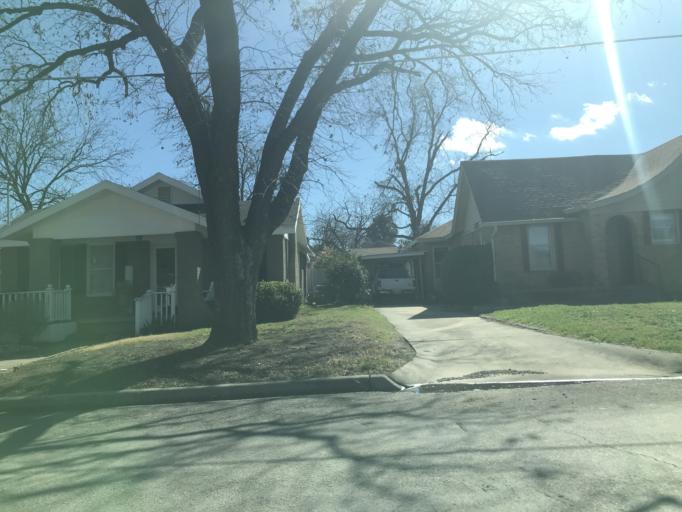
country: US
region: Texas
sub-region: Tom Green County
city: San Angelo
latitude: 31.4475
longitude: -100.4581
